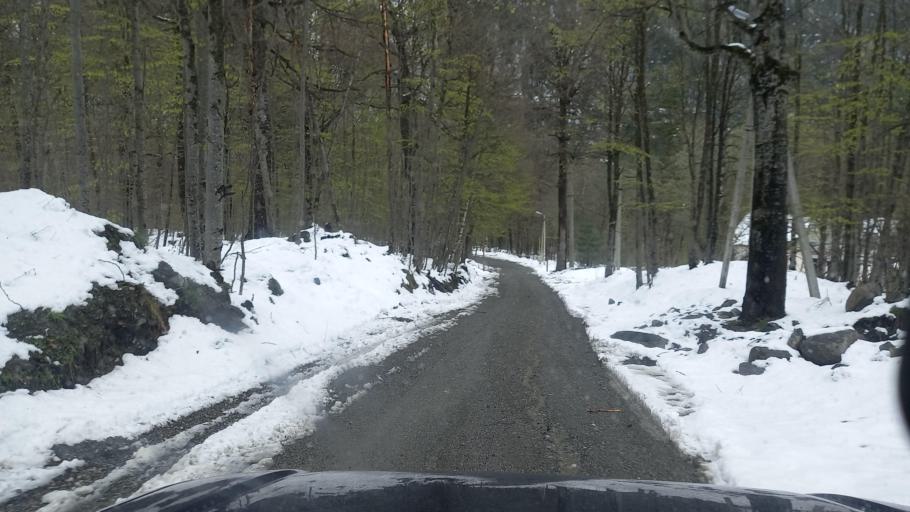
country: RU
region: North Ossetia
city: Mizur
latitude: 42.7870
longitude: 43.9032
